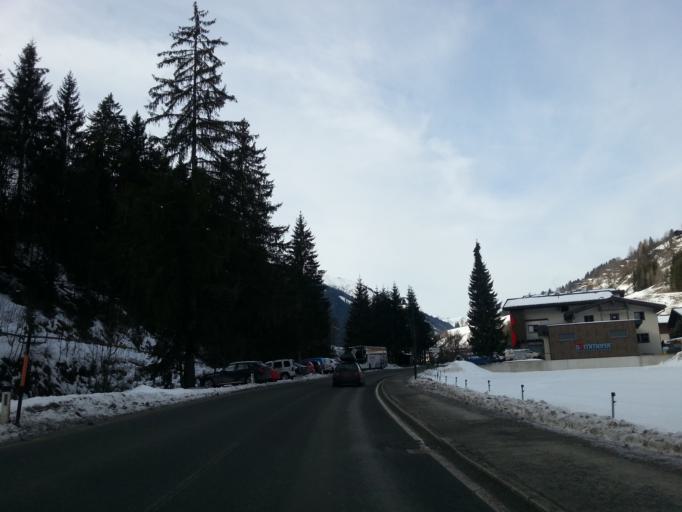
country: AT
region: Salzburg
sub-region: Politischer Bezirk Zell am See
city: Saalbach
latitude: 47.3847
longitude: 12.6132
